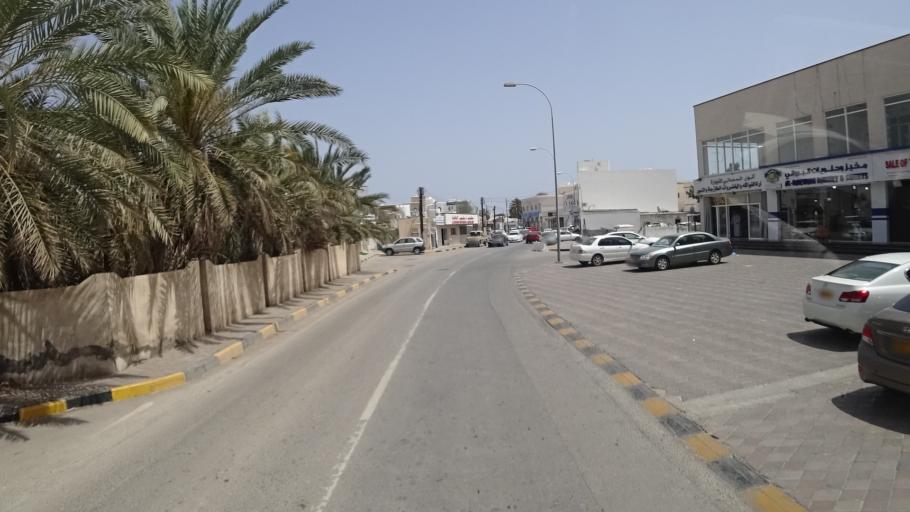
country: OM
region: Muhafazat Masqat
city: Muscat
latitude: 23.2588
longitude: 58.9141
